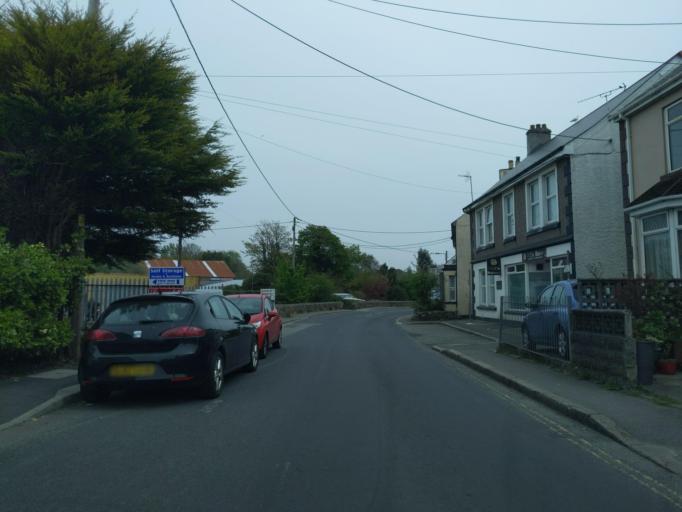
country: GB
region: England
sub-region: Cornwall
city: Par
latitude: 50.3506
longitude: -4.7095
